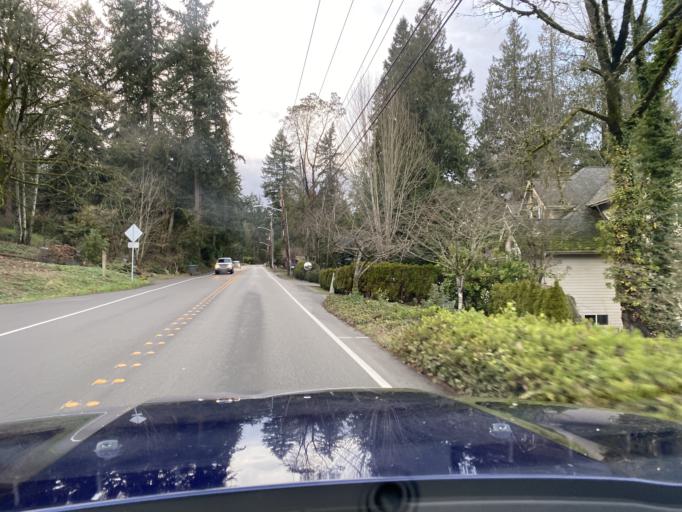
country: US
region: Washington
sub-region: King County
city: West Lake Sammamish
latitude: 47.5703
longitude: -122.1127
